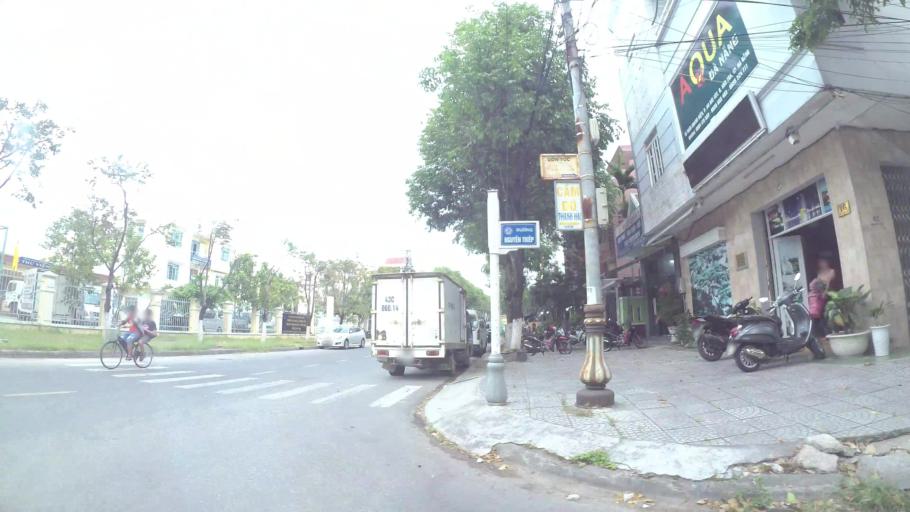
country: VN
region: Da Nang
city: Son Tra
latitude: 16.0545
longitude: 108.2343
